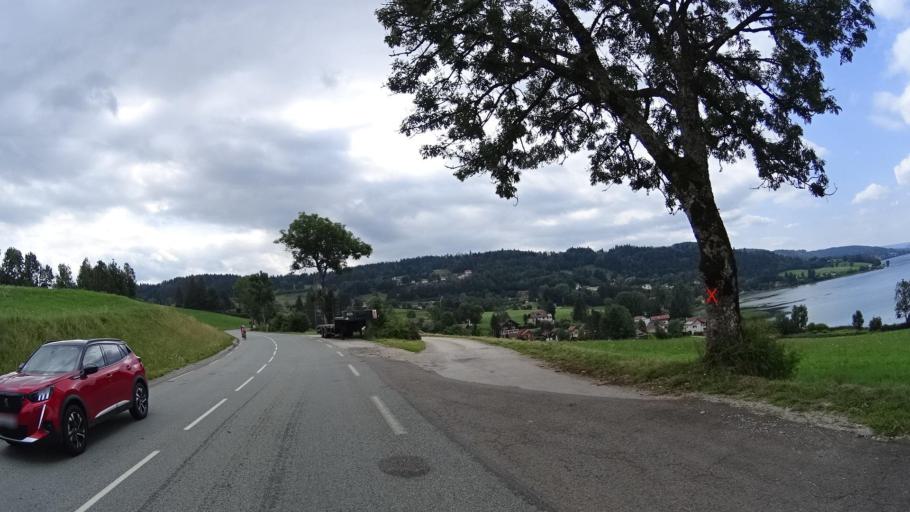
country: FR
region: Franche-Comte
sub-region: Departement du Doubs
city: Les Fourgs
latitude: 46.8391
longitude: 6.3397
